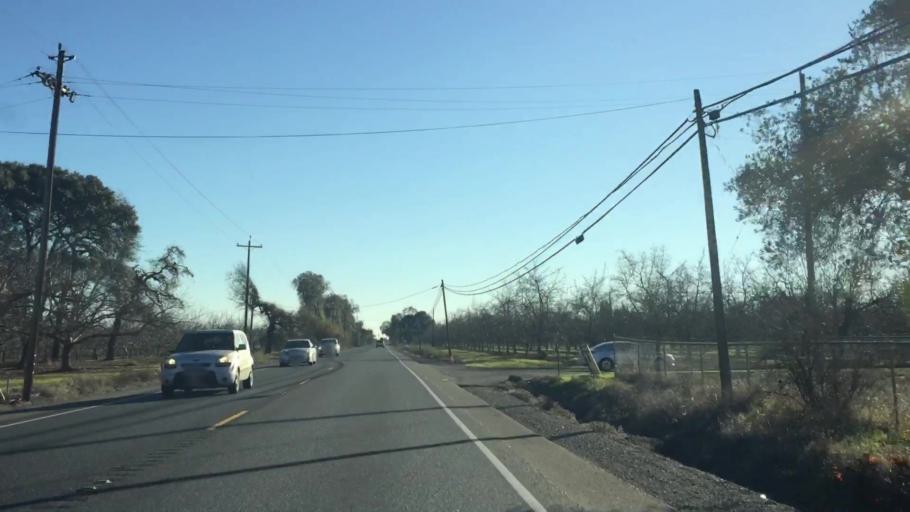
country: US
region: California
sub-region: Sutter County
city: Live Oak
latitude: 39.2346
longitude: -121.6004
